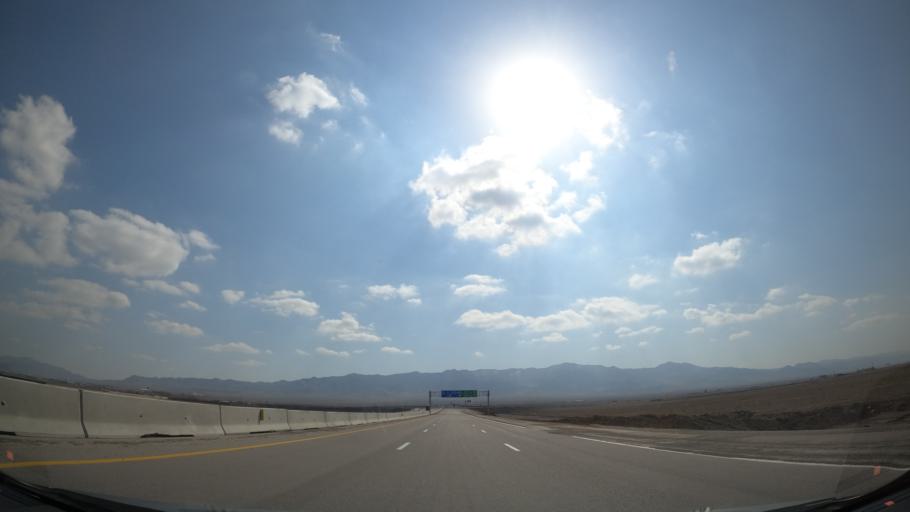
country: IR
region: Alborz
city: Eshtehard
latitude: 35.7405
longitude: 50.5608
